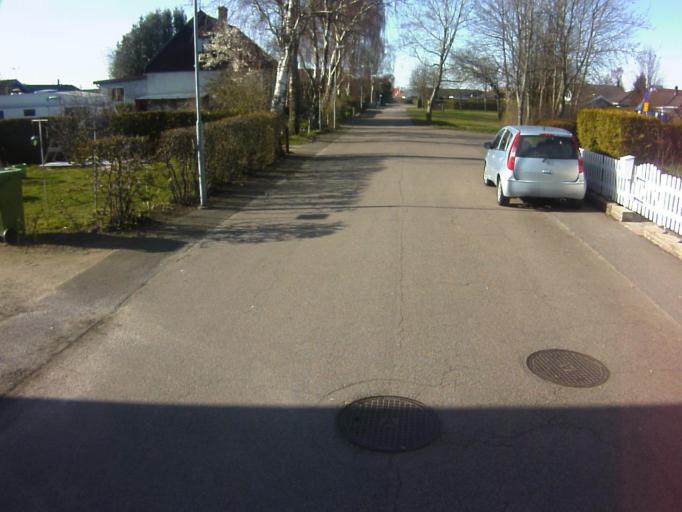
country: SE
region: Skane
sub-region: Kavlinge Kommun
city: Kaevlinge
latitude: 55.8033
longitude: 13.1079
